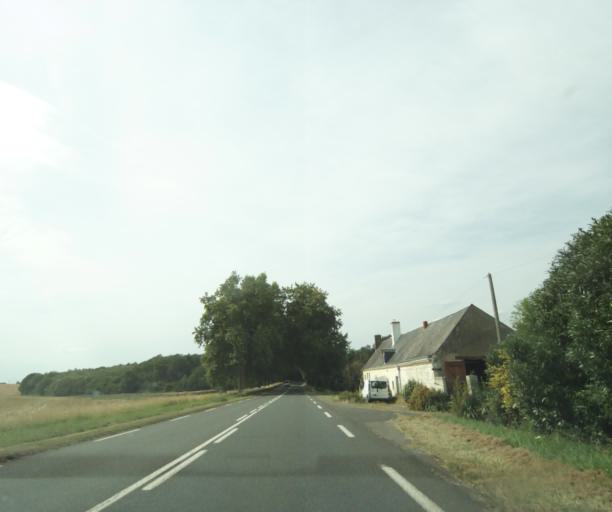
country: FR
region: Centre
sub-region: Departement d'Indre-et-Loire
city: Saint-Paterne-Racan
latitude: 47.6104
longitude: 0.5103
